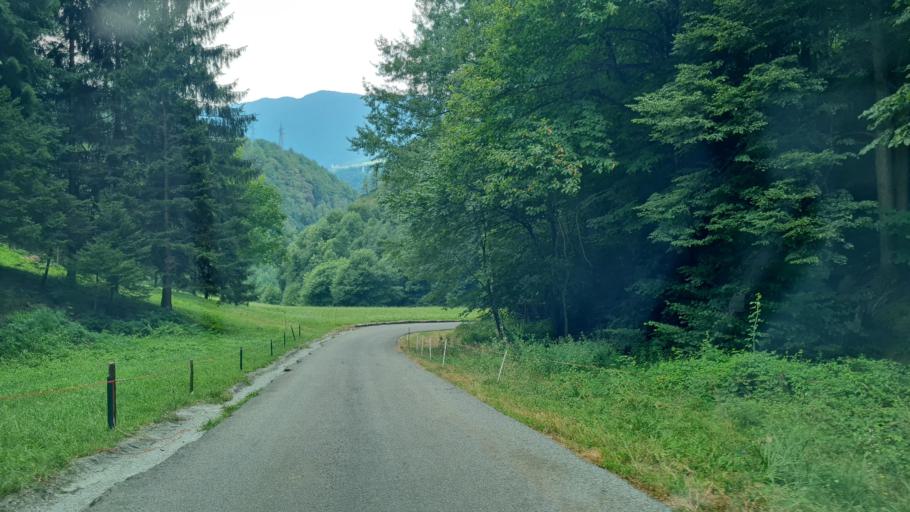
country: IT
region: Piedmont
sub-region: Provincia Verbano-Cusio-Ossola
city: Premia
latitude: 46.2636
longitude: 8.3391
